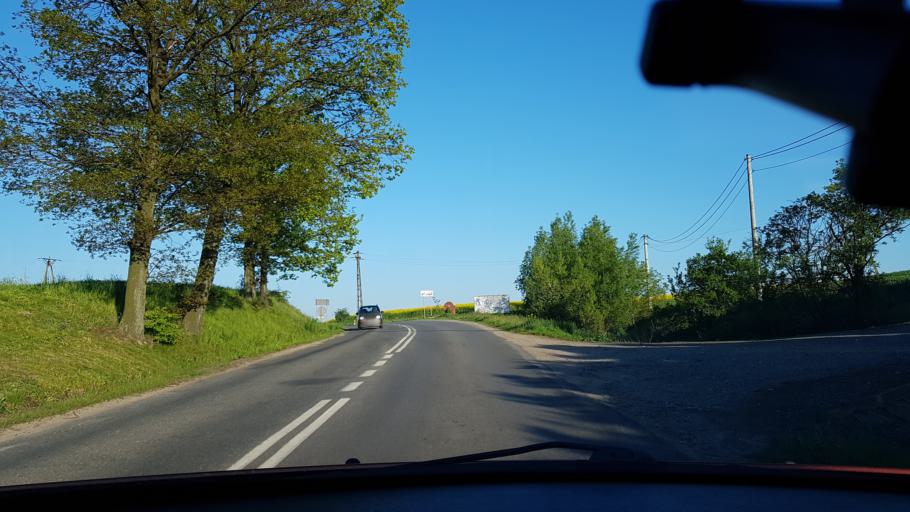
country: PL
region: Lower Silesian Voivodeship
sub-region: Powiat zabkowicki
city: Stoszowice
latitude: 50.6007
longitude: 16.7525
